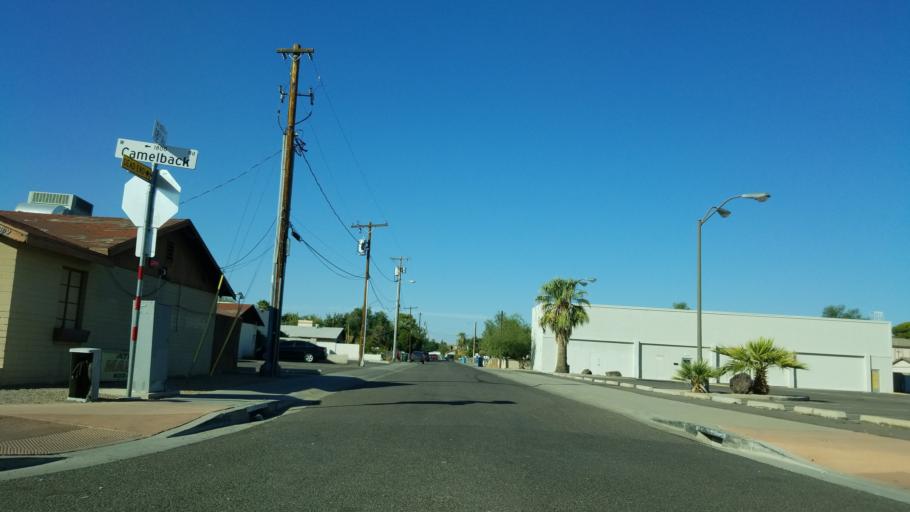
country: US
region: Arizona
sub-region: Maricopa County
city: Phoenix
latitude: 33.5097
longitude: -112.0975
